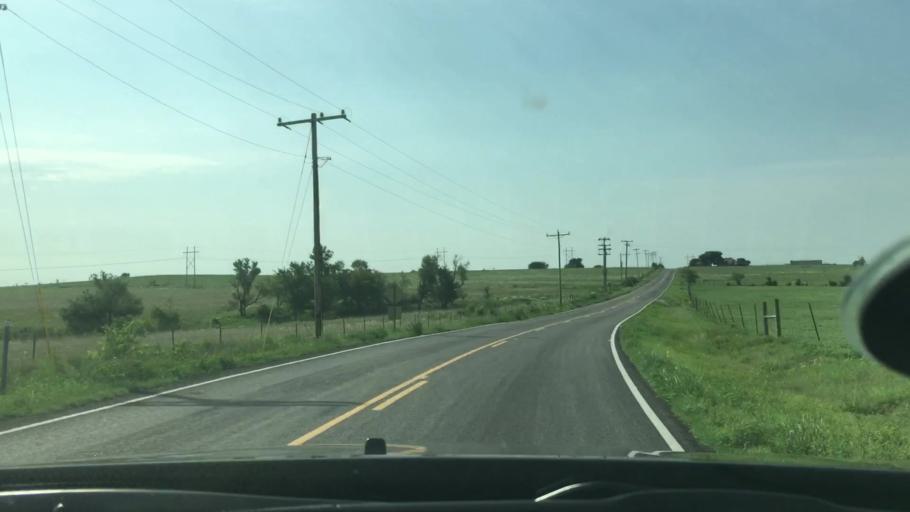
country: US
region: Oklahoma
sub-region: Bryan County
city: Durant
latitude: 34.1417
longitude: -96.4970
